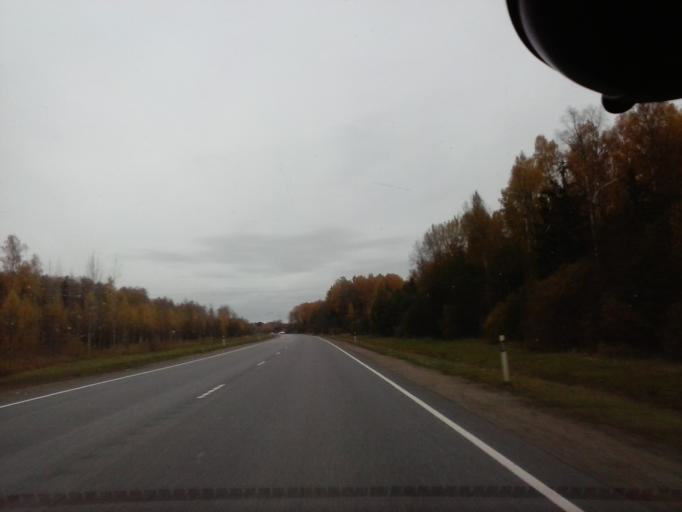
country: EE
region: Tartu
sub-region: Puhja vald
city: Puhja
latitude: 58.5017
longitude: 26.3298
